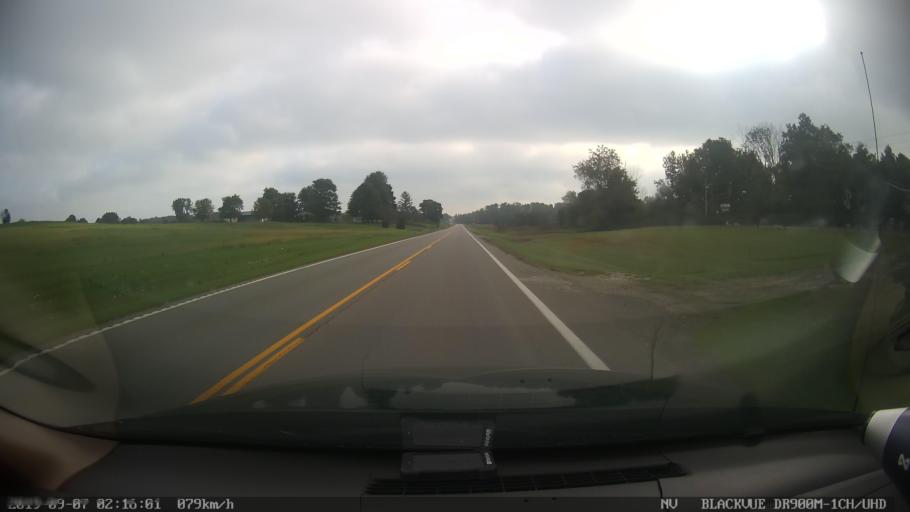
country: US
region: Ohio
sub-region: Licking County
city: Utica
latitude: 40.2180
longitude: -82.5452
